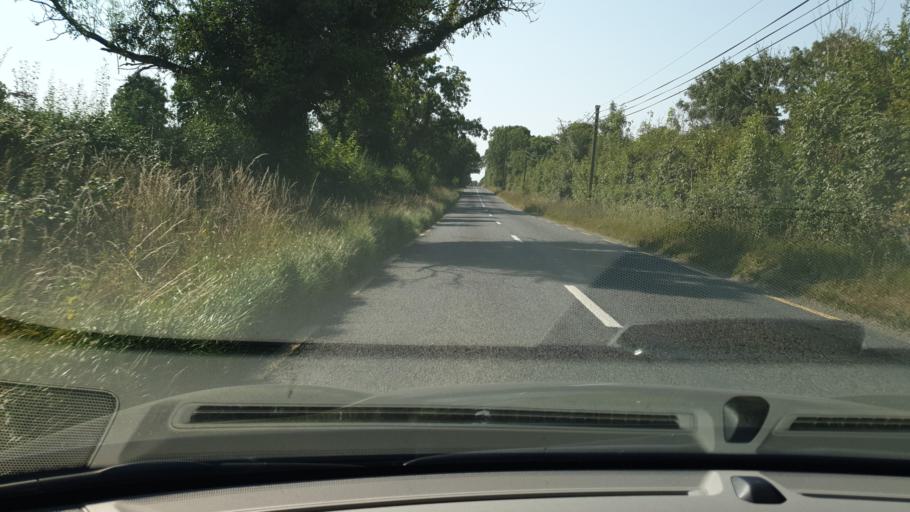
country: IE
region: Leinster
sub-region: Kildare
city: Kilcock
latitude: 53.4779
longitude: -6.7055
